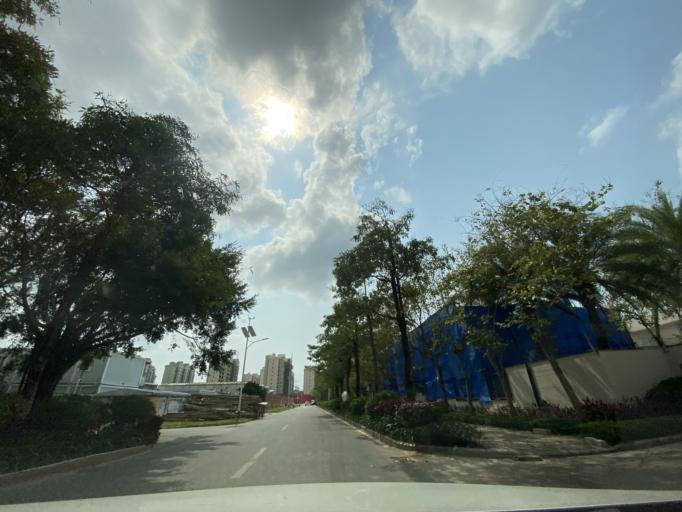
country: CN
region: Hainan
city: Yingzhou
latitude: 18.4098
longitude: 109.8535
